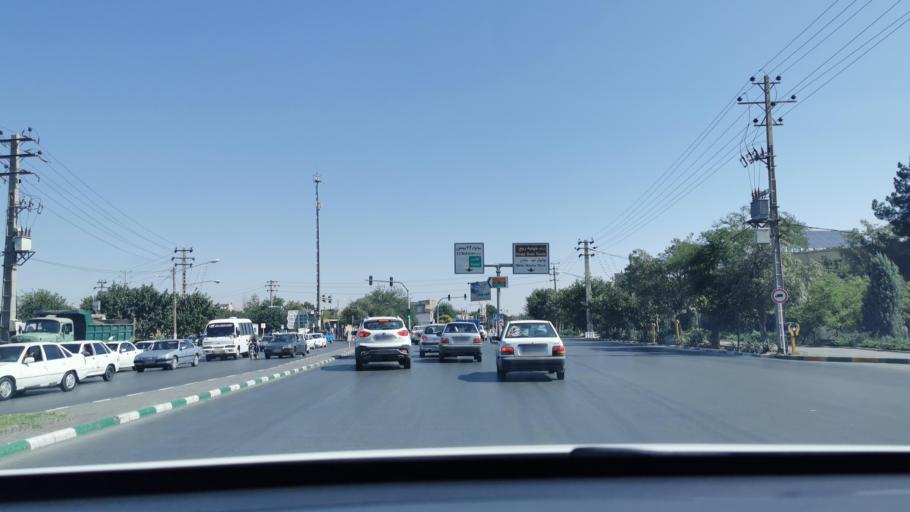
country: IR
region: Razavi Khorasan
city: Mashhad
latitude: 36.3367
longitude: 59.6260
